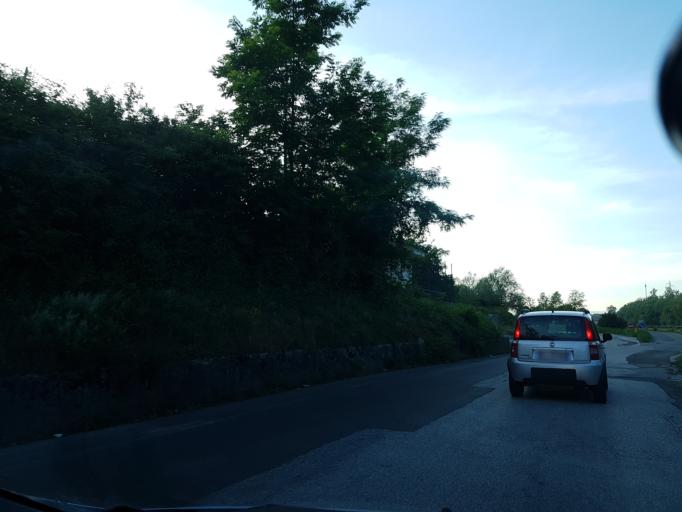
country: IT
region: Tuscany
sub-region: Provincia di Massa-Carrara
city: Aulla
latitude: 44.2144
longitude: 9.9775
